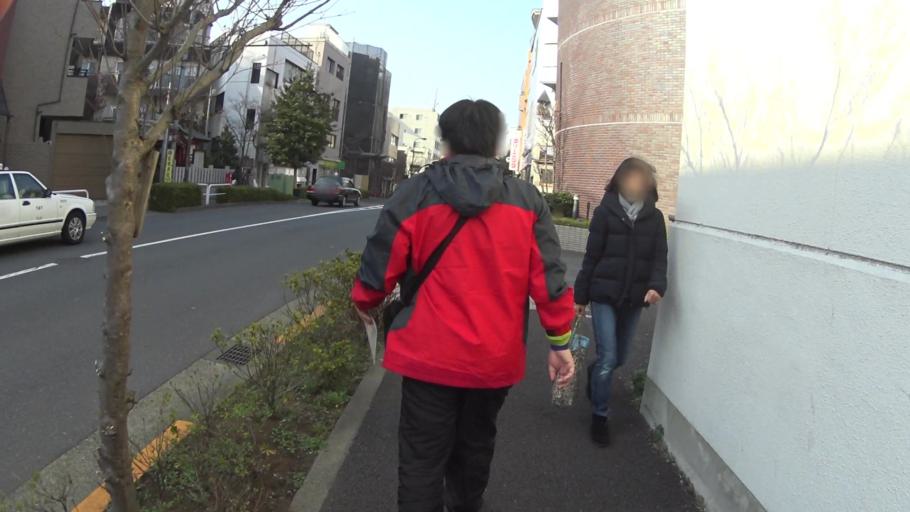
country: JP
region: Tokyo
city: Tokyo
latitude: 35.6393
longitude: 139.7126
